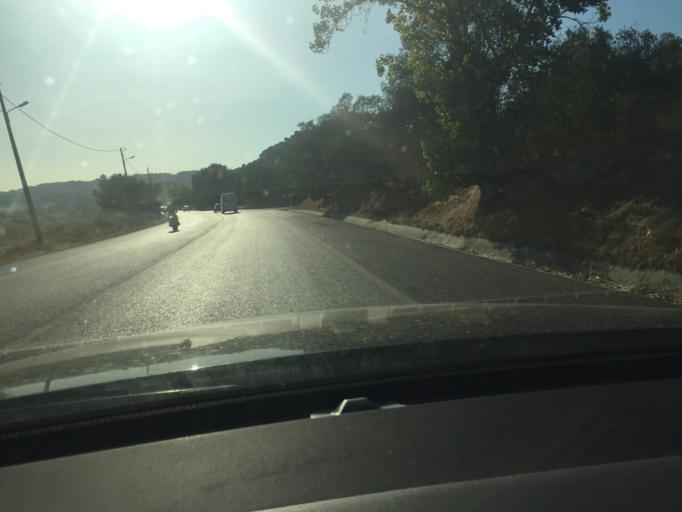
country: PT
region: Setubal
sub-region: Palmela
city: Quinta do Anjo
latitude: 38.5251
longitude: -8.9406
